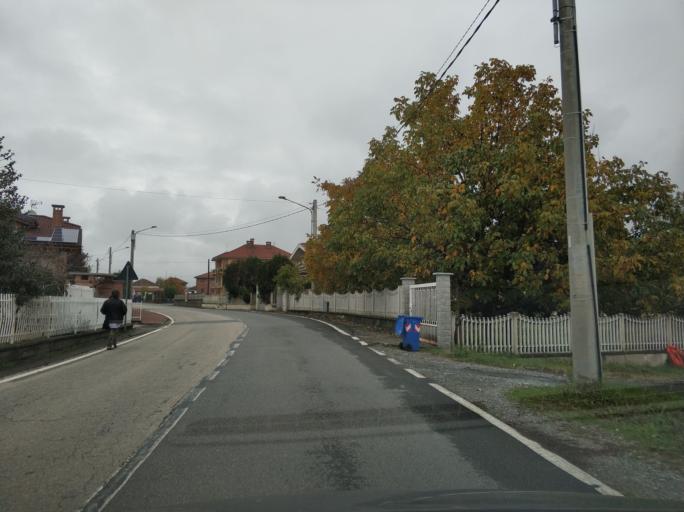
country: IT
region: Piedmont
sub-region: Provincia di Torino
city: Villanova Canavese
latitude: 45.2461
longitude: 7.5560
